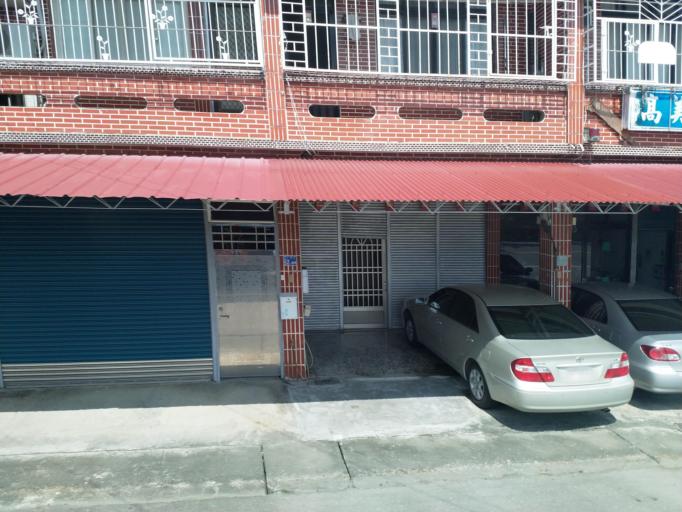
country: TW
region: Taiwan
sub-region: Pingtung
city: Pingtung
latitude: 22.8805
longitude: 120.5617
